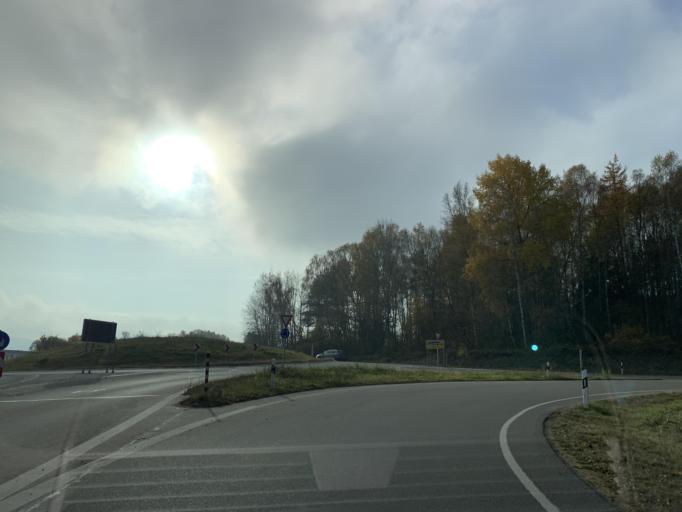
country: DE
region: Bavaria
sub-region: Upper Palatinate
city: Bruck in der Oberpfalz
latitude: 49.2511
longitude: 12.2959
